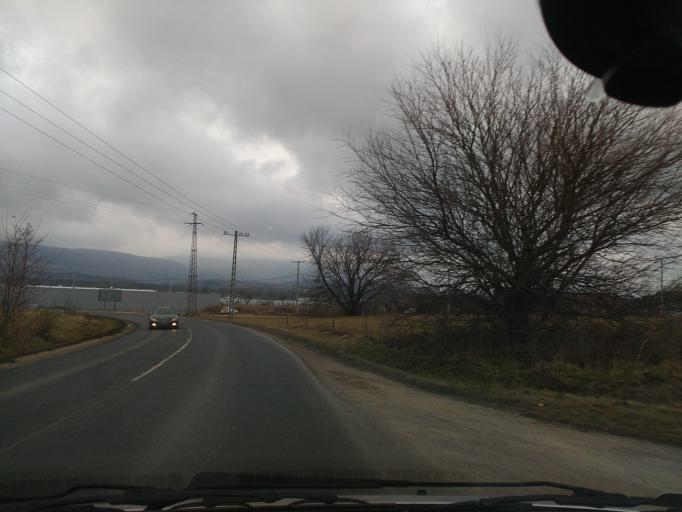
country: HU
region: Komarom-Esztergom
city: Dorog
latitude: 47.7099
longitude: 18.7385
